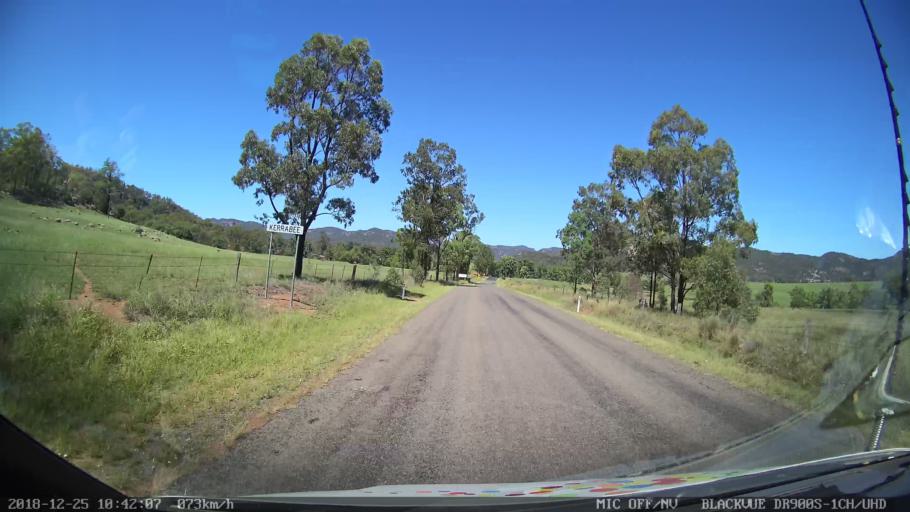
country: AU
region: New South Wales
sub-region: Upper Hunter Shire
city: Merriwa
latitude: -32.4147
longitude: 150.3275
